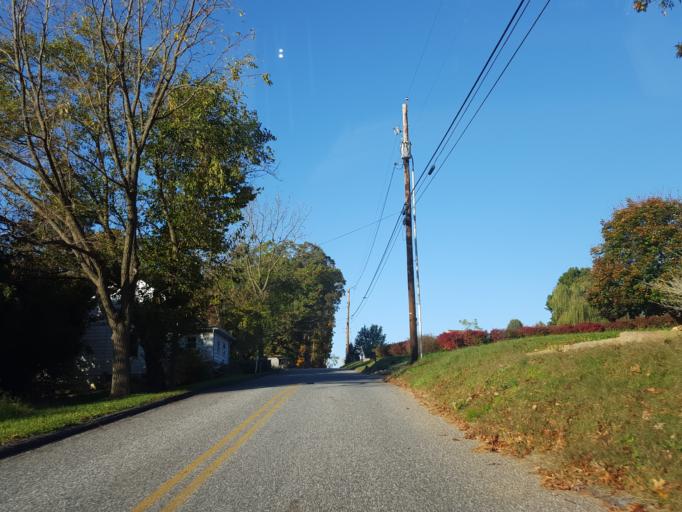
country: US
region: Pennsylvania
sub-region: York County
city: Yoe
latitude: 39.9343
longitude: -76.6396
